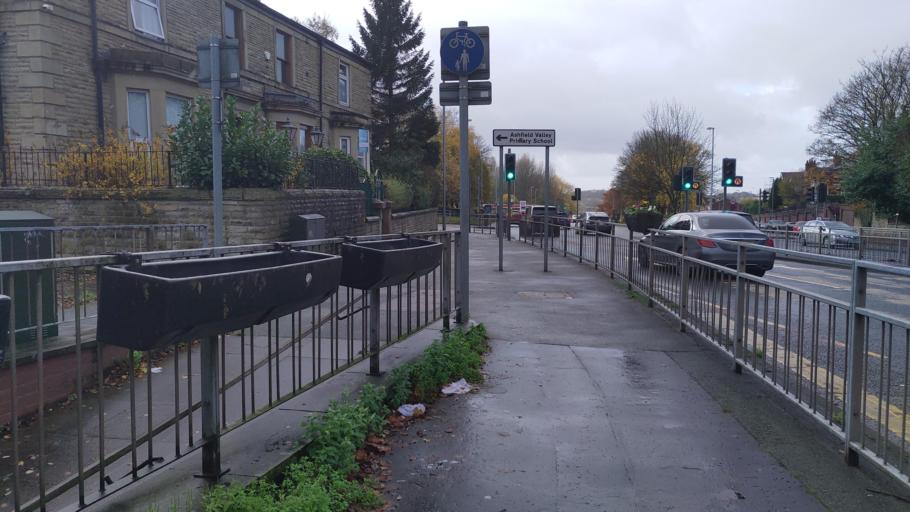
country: GB
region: England
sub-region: Borough of Rochdale
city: Rochdale
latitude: 53.6057
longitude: -2.1672
